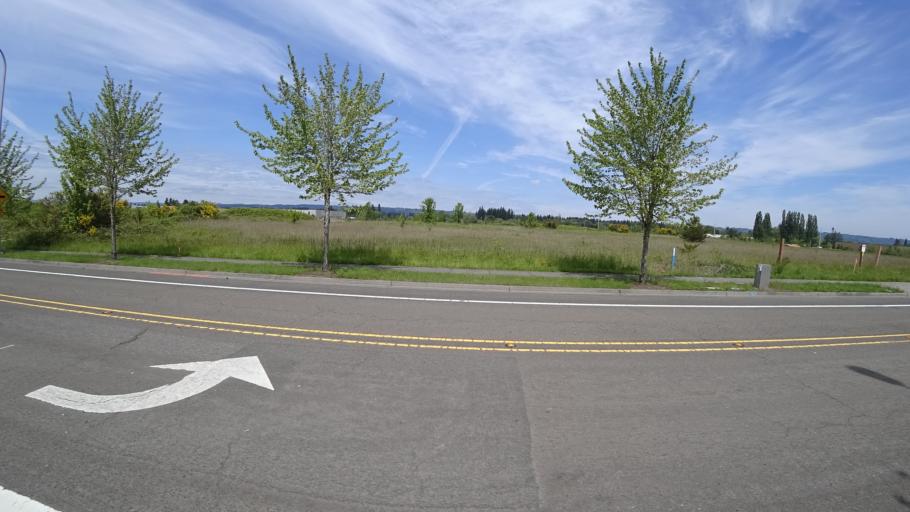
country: US
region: Oregon
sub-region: Washington County
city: Rockcreek
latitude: 45.5653
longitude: -122.9040
